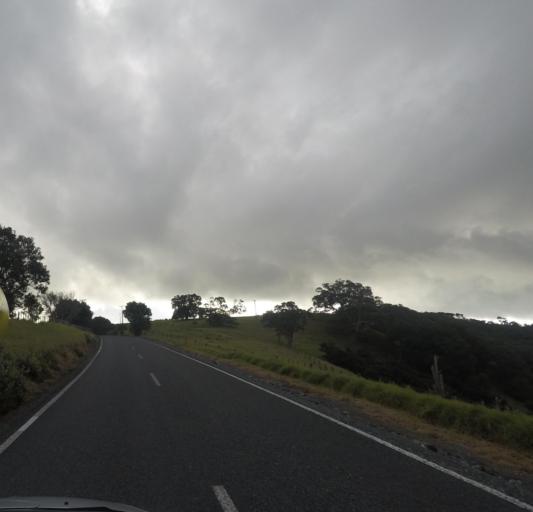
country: NZ
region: Auckland
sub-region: Auckland
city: Warkworth
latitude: -36.3781
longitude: 174.8165
